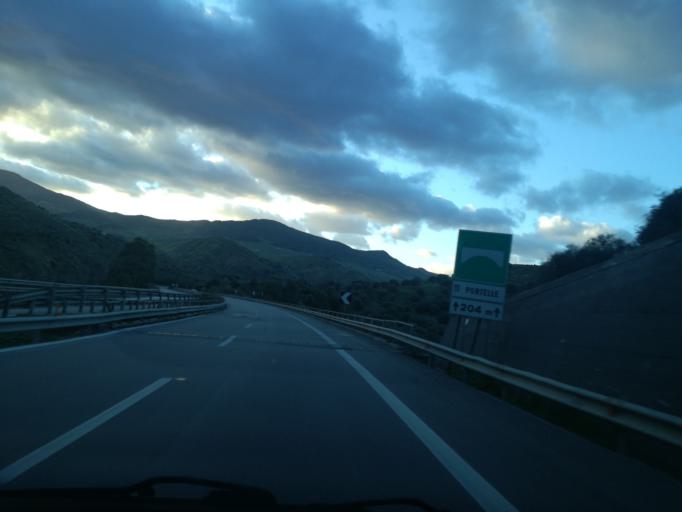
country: IT
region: Sicily
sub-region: Palermo
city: Scillato
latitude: 37.8638
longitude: 13.8845
